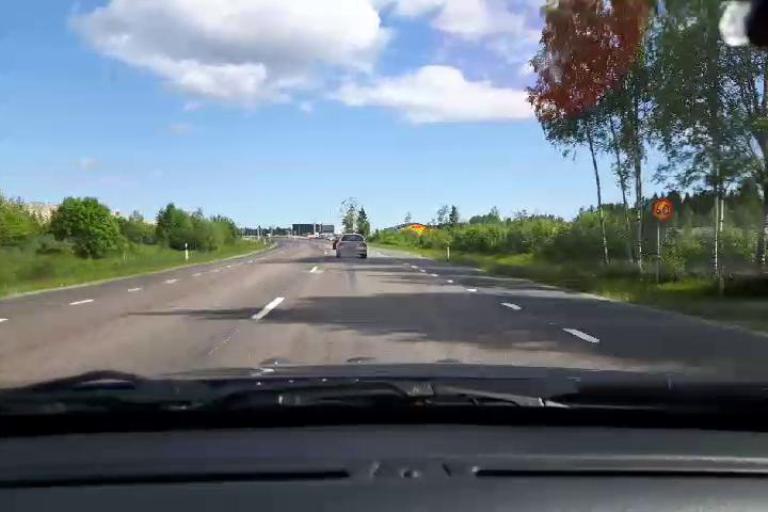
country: SE
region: Gaevleborg
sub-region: Hudiksvalls Kommun
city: Sorforsa
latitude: 61.7154
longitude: 17.0371
